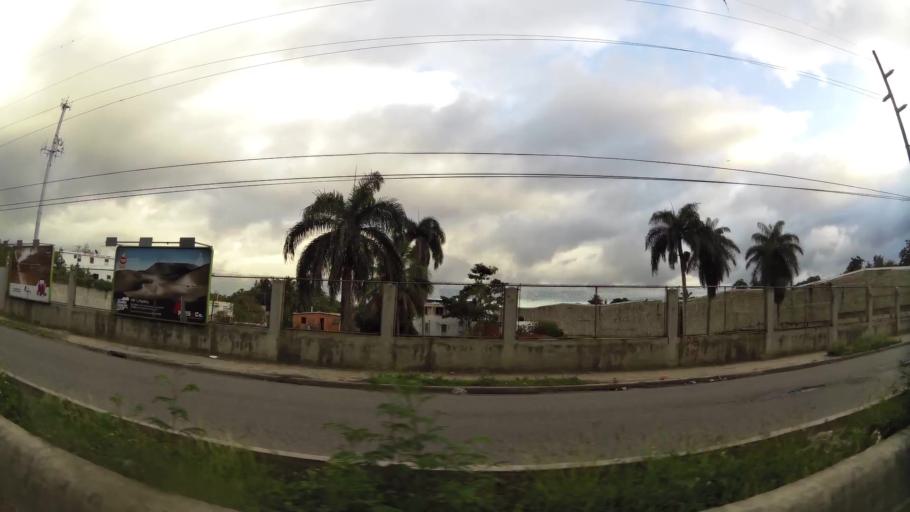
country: DO
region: Santo Domingo
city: Santo Domingo Oeste
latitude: 18.5074
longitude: -69.9973
